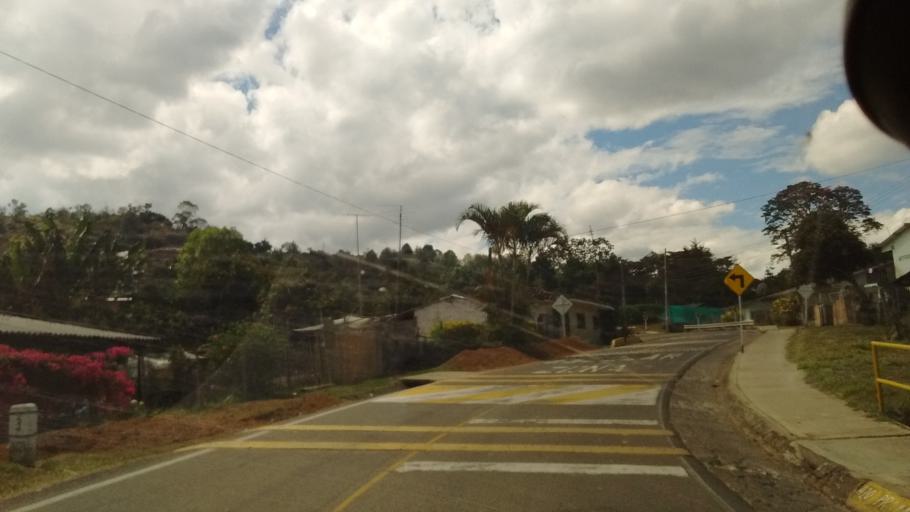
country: CO
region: Cauca
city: Cajibio
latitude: 2.6274
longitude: -76.5164
